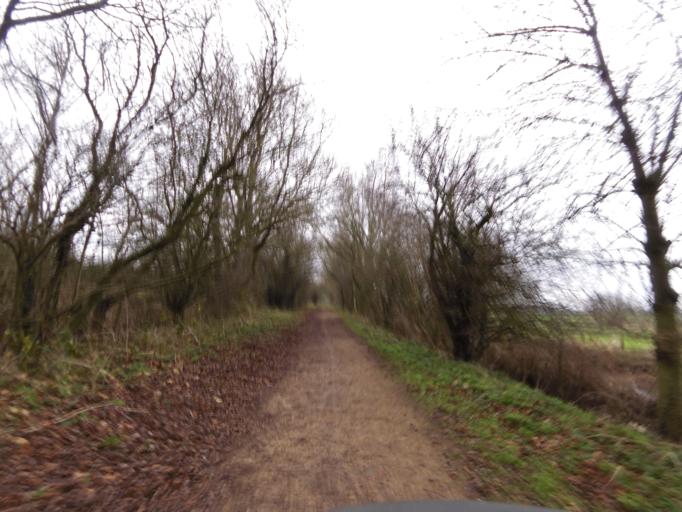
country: GB
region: England
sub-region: Norfolk
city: Mattishall
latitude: 52.7331
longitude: 1.1006
